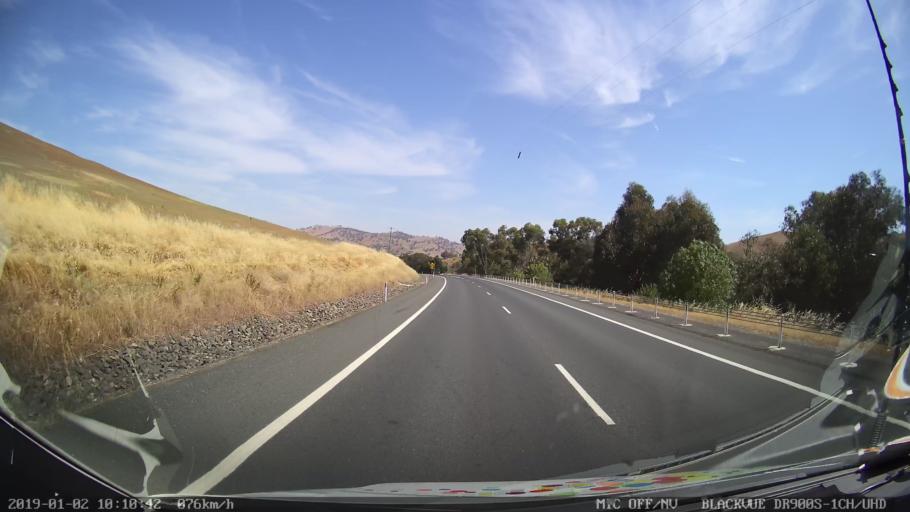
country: AU
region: New South Wales
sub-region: Gundagai
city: Gundagai
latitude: -35.1007
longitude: 148.0958
